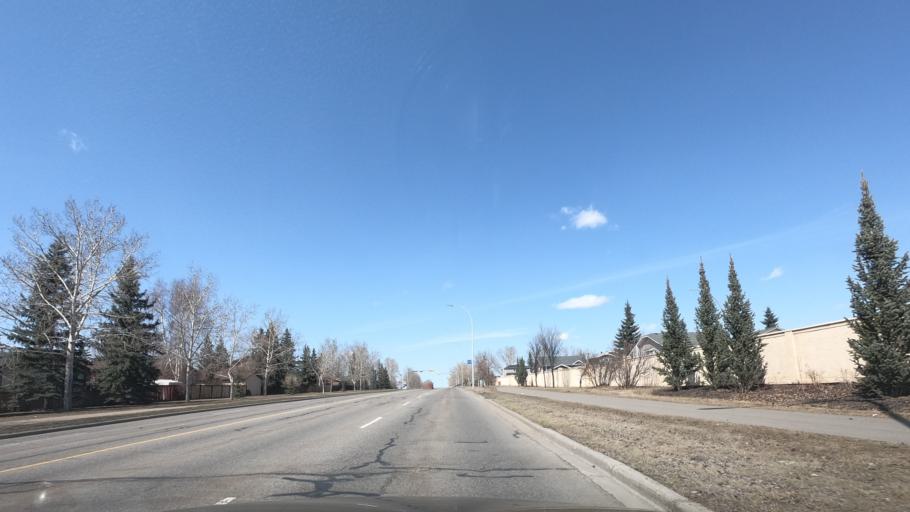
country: CA
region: Alberta
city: Airdrie
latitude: 51.2786
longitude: -113.9898
